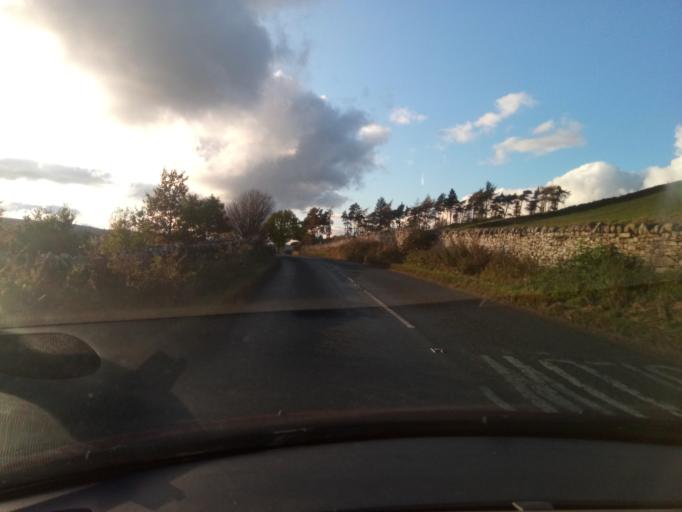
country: GB
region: England
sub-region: County Durham
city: Newbiggin
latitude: 54.7373
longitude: -2.1214
